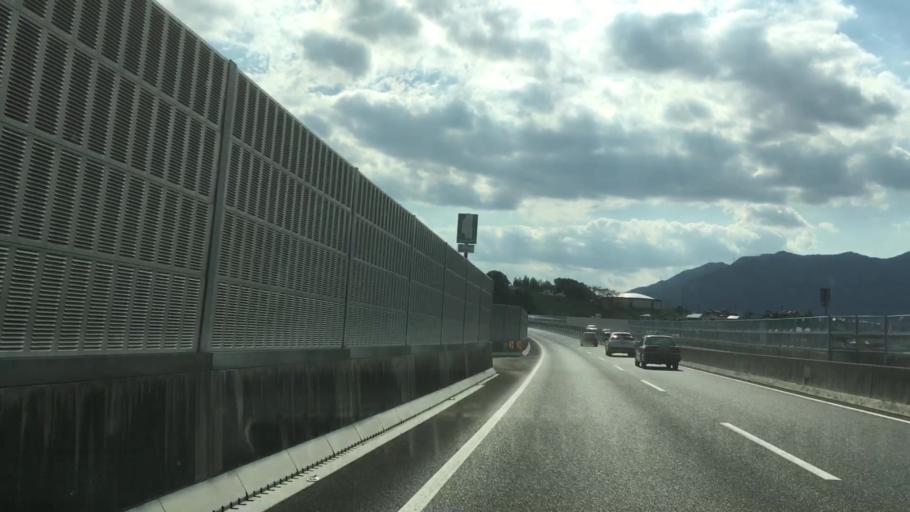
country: JP
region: Hiroshima
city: Hatsukaichi
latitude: 34.3572
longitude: 132.3252
